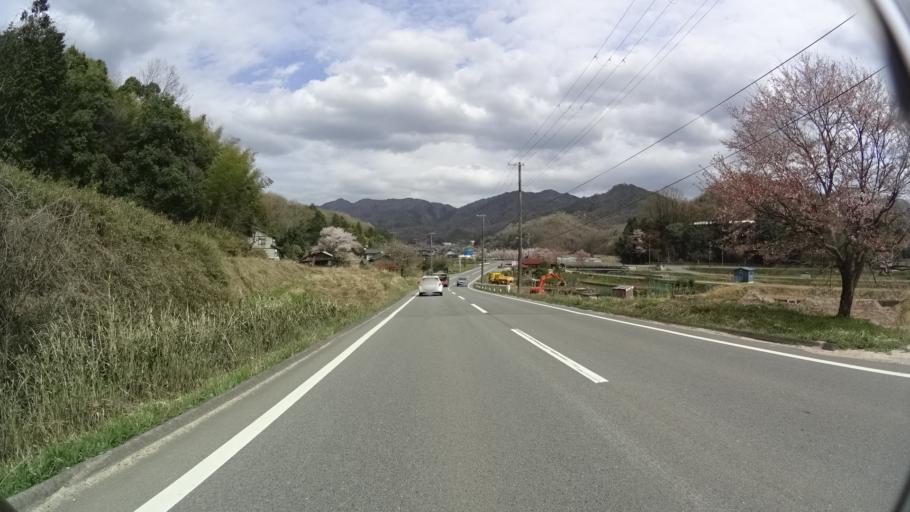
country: JP
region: Hyogo
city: Toyooka
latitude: 35.5024
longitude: 134.8741
